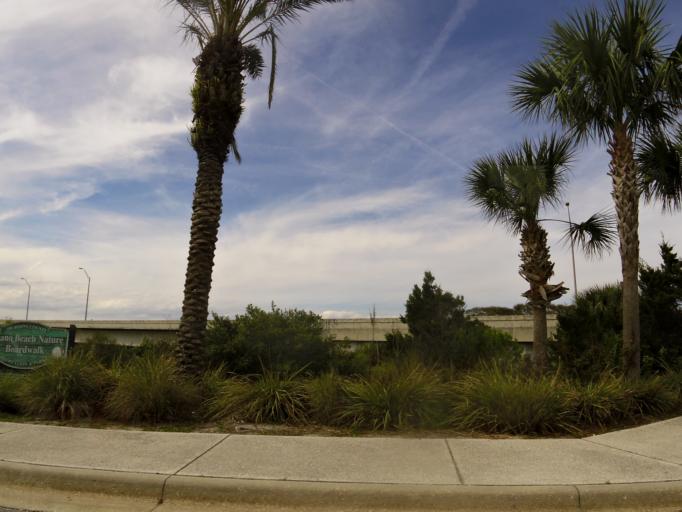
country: US
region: Florida
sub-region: Saint Johns County
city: Villano Beach
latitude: 29.9177
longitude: -81.2946
